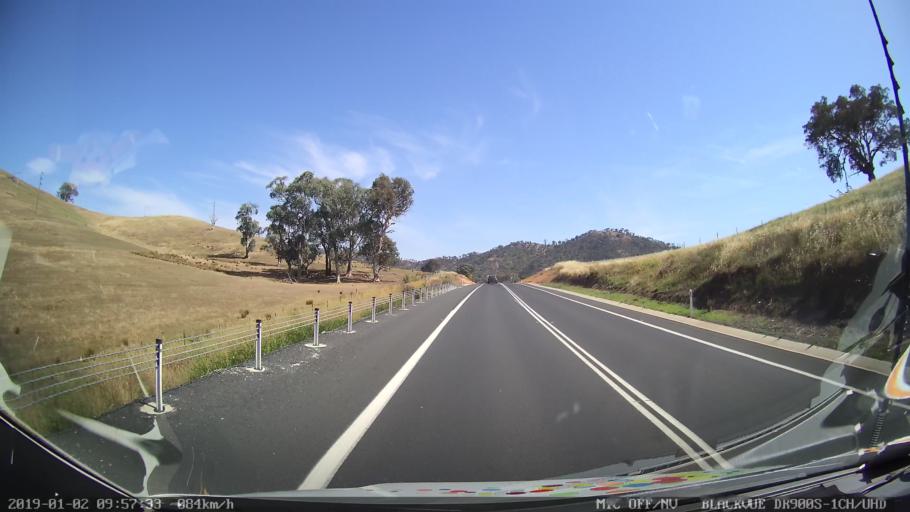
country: AU
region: New South Wales
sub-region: Tumut Shire
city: Tumut
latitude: -35.2040
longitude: 148.1655
